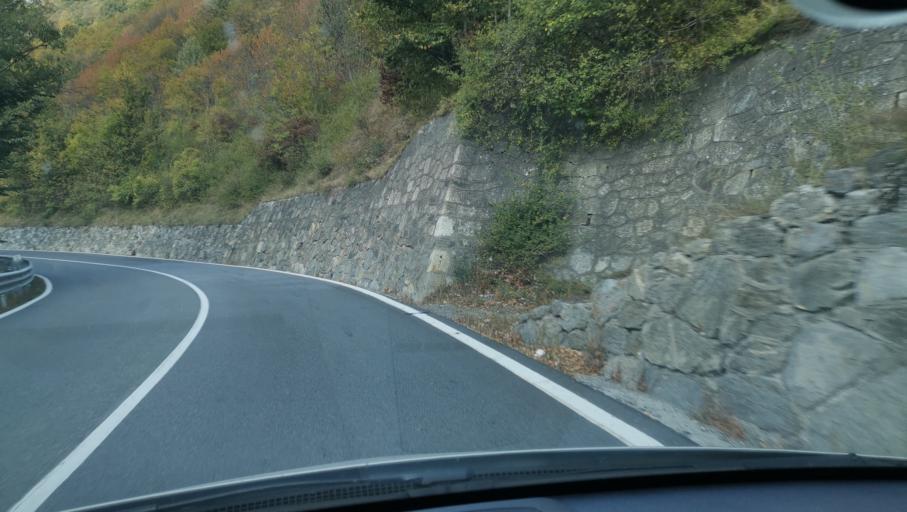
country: IT
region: Piedmont
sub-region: Provincia di Torino
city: Salbertrand
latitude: 45.0793
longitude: 6.8957
